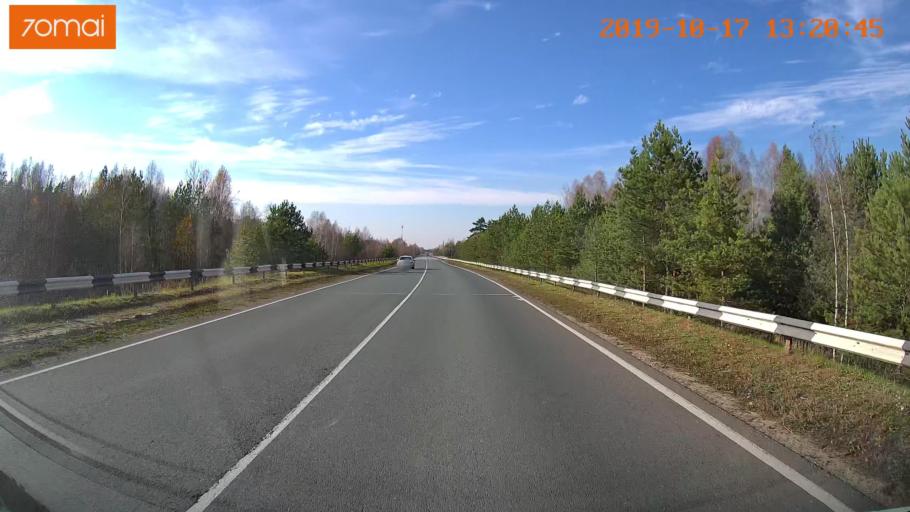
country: RU
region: Rjazan
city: Gus'-Zheleznyy
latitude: 55.0783
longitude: 41.0437
